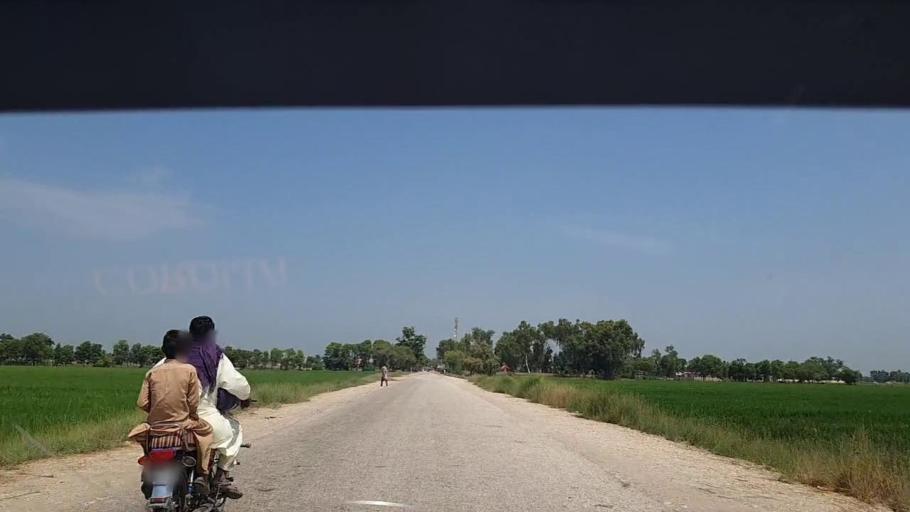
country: PK
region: Sindh
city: Rustam jo Goth
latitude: 28.0748
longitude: 68.7833
